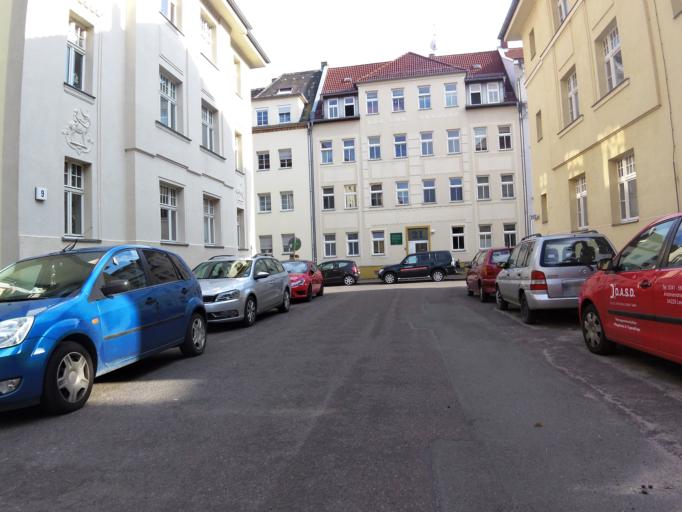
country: DE
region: Saxony
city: Leipzig
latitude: 51.3146
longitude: 12.3226
